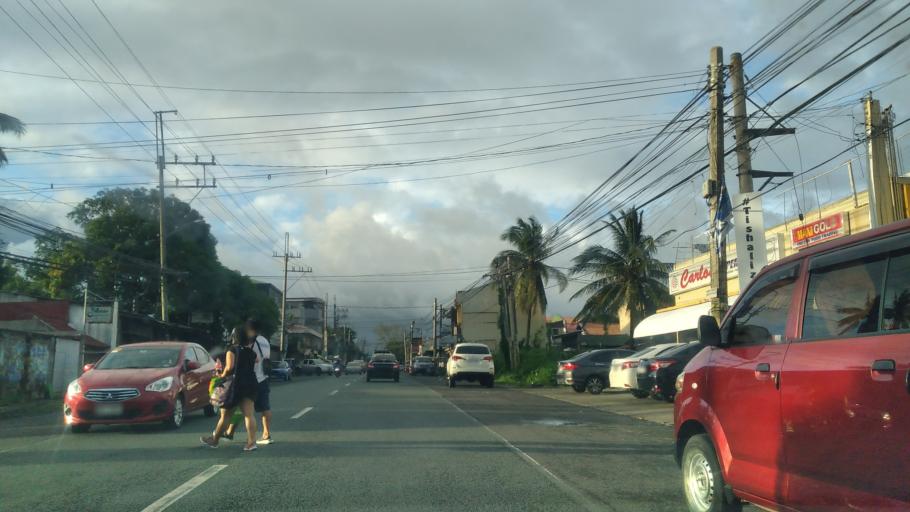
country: PH
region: Calabarzon
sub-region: Province of Quezon
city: Lucena
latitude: 13.9516
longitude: 121.6130
